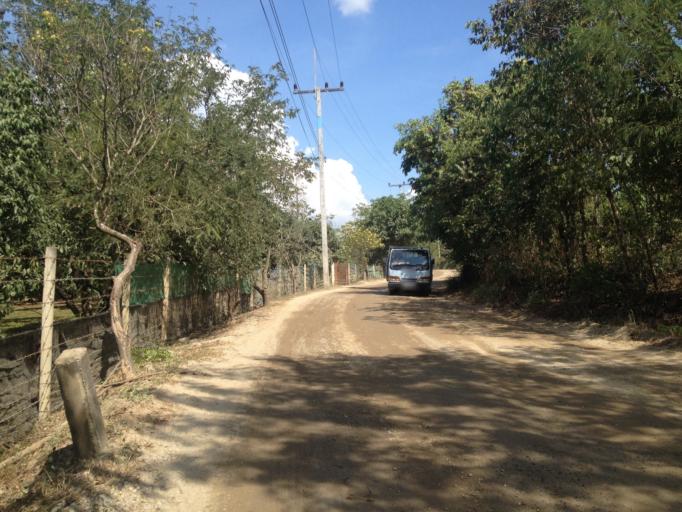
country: TH
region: Chiang Mai
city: Hang Dong
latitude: 18.6946
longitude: 98.8722
